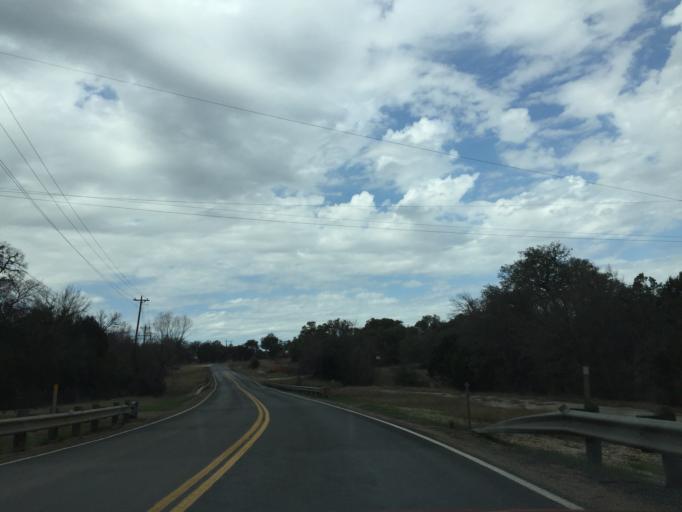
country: US
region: Texas
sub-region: Burnet County
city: Bertram
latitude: 30.7150
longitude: -97.9280
